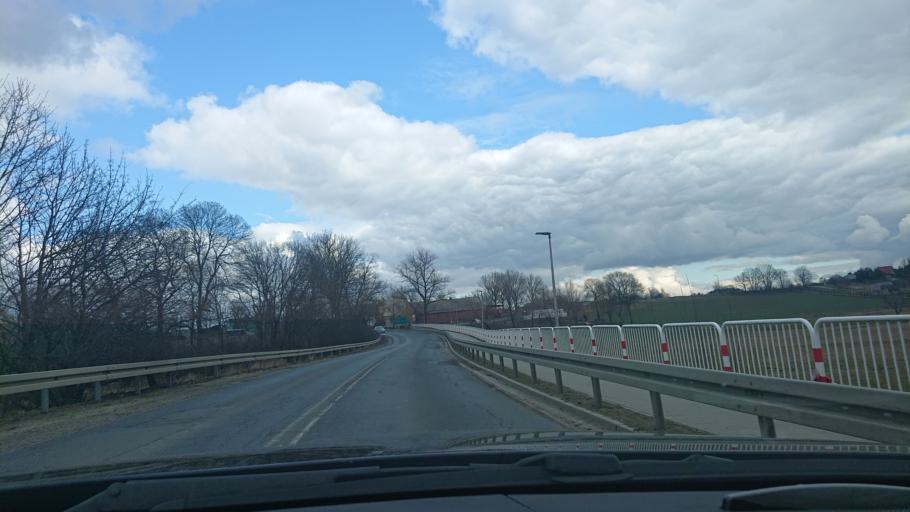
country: PL
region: Greater Poland Voivodeship
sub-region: Powiat gnieznienski
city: Niechanowo
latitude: 52.5520
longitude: 17.6953
